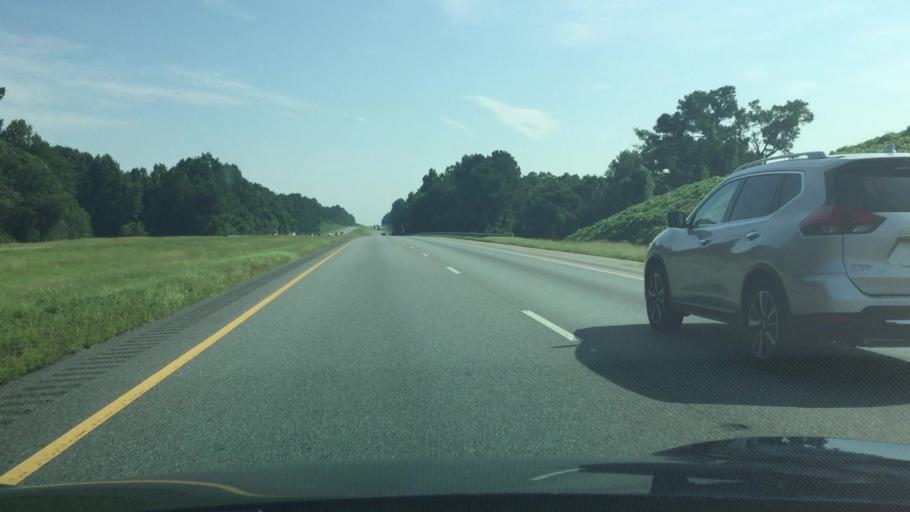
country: US
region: Alabama
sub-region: Lowndes County
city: Fort Deposit
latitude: 31.9240
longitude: -86.5759
